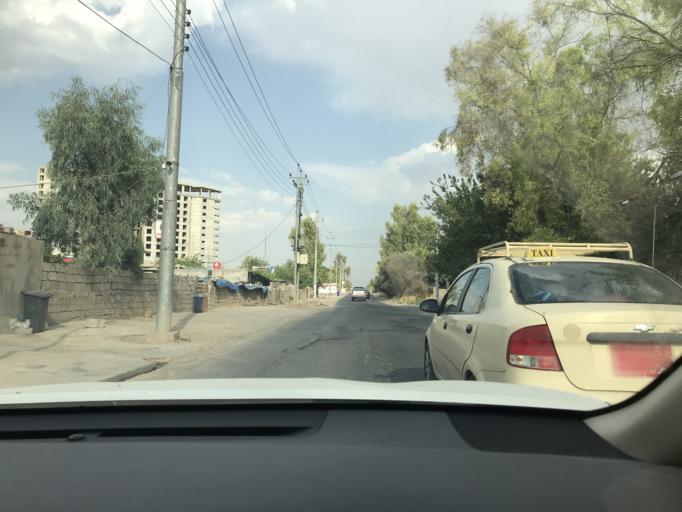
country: IQ
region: Arbil
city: Erbil
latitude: 36.2082
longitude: 43.9560
